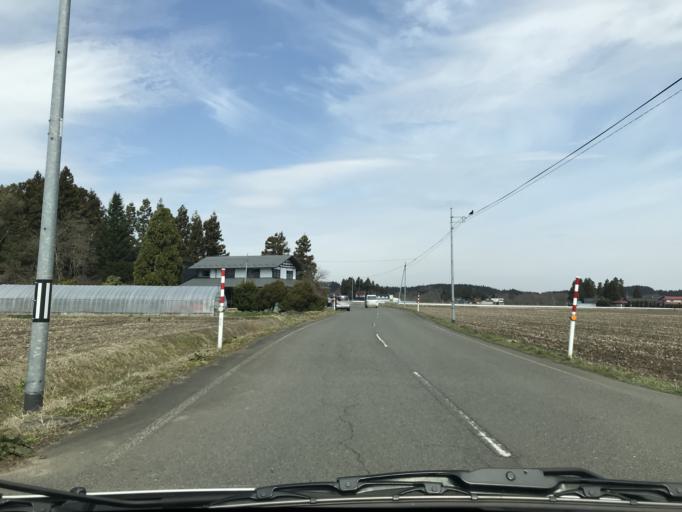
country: JP
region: Iwate
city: Mizusawa
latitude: 39.1421
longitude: 141.0583
